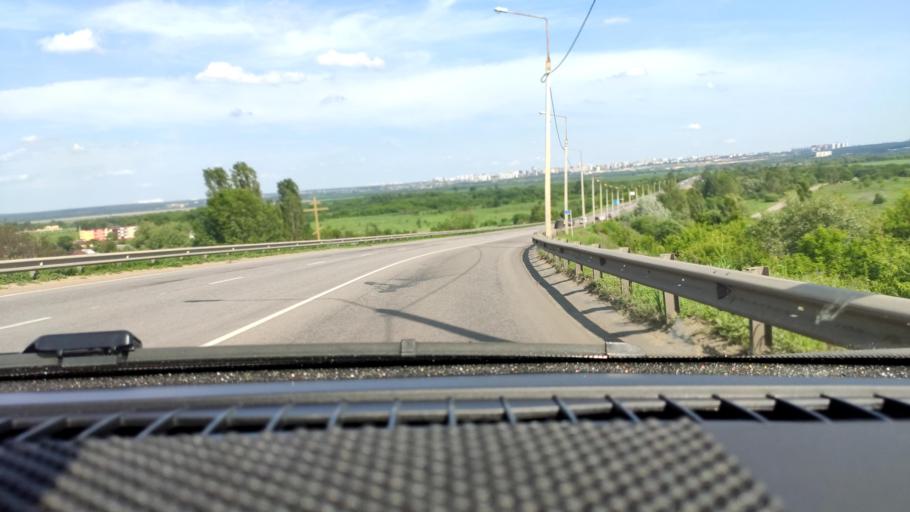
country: RU
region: Voronezj
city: Semiluki
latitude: 51.7266
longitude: 39.0487
